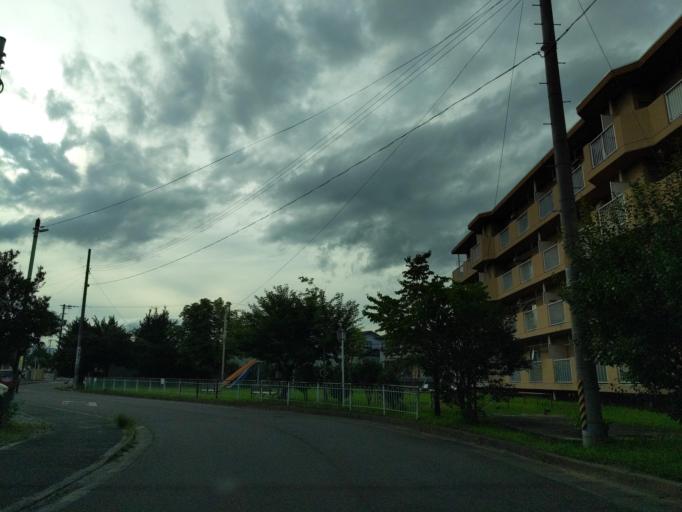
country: JP
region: Fukushima
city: Koriyama
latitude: 37.4046
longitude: 140.3334
